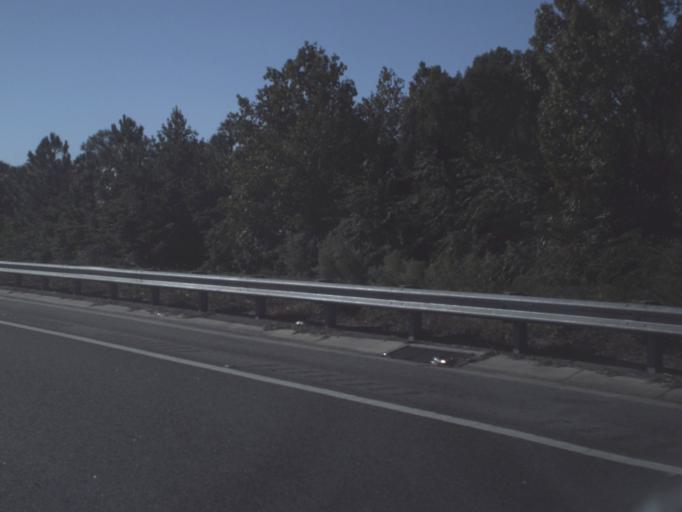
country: US
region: Florida
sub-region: Seminole County
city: Midway
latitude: 28.7361
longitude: -81.2534
